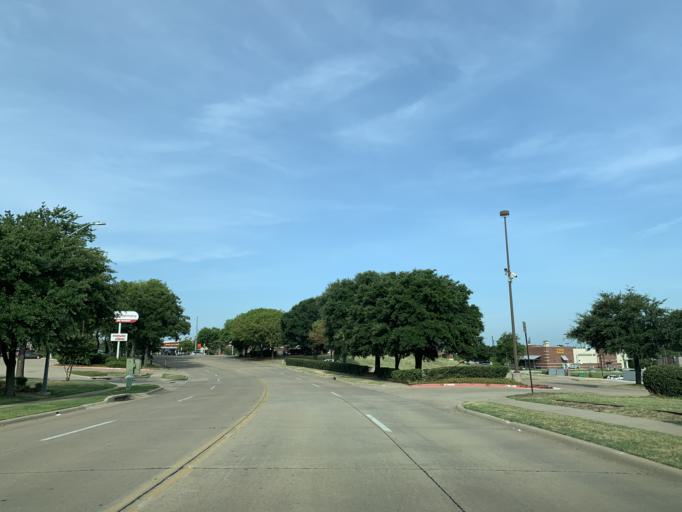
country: US
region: Texas
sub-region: Dallas County
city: Grand Prairie
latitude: 32.6721
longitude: -97.0040
